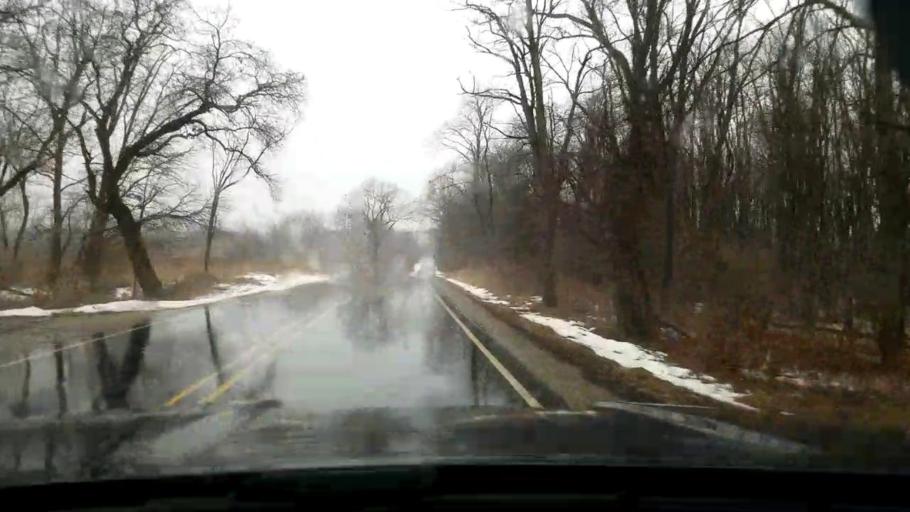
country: US
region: Michigan
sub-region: Jackson County
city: Grass Lake
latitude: 42.3319
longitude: -84.1851
